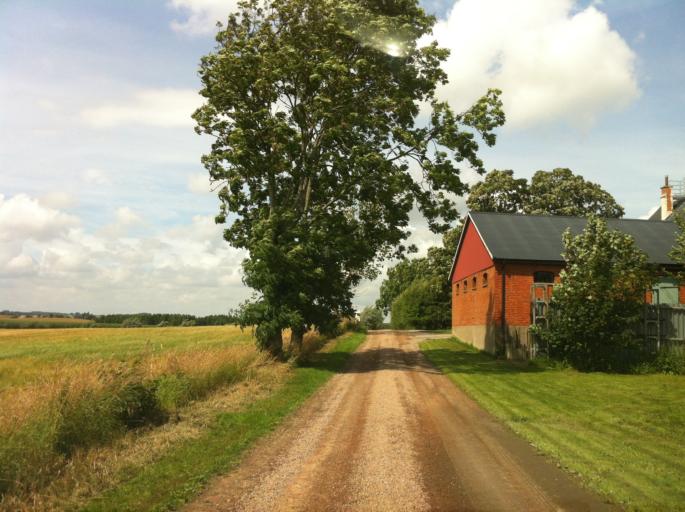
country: SE
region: Skane
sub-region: Skurups Kommun
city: Skurup
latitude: 55.4444
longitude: 13.4391
